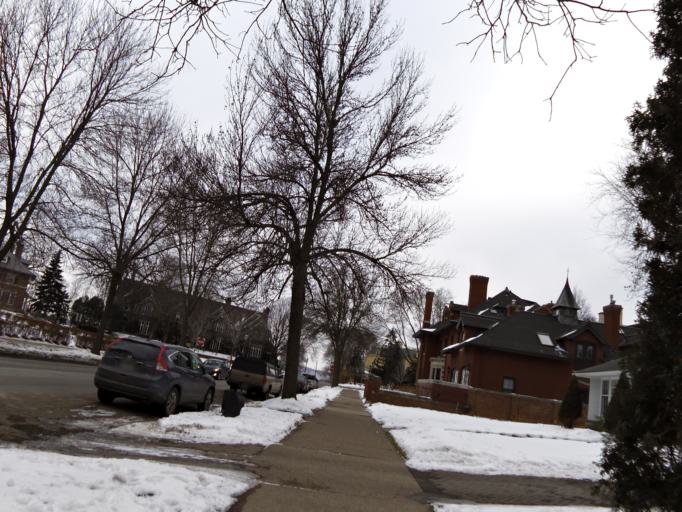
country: US
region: Minnesota
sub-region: Ramsey County
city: Saint Paul
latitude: 44.9432
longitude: -93.1162
